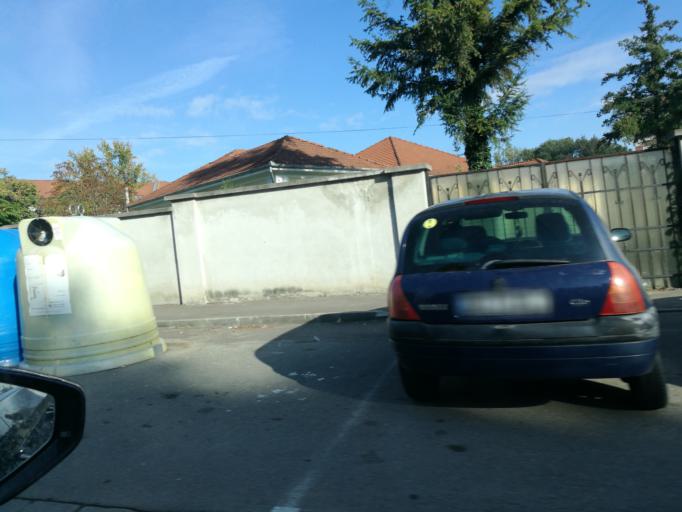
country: RO
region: Bihor
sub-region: Comuna Biharea
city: Oradea
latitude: 47.0422
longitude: 21.9201
